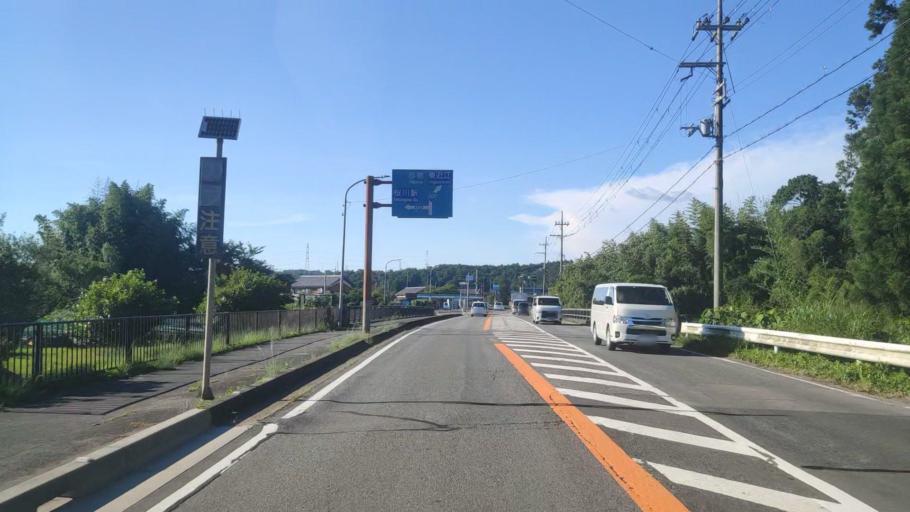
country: JP
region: Shiga Prefecture
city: Hino
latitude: 35.0517
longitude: 136.2388
